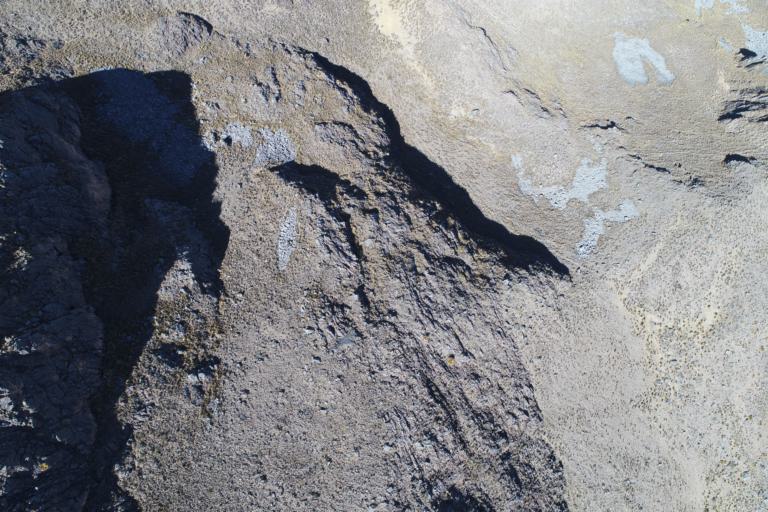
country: BO
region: La Paz
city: Viloco
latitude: -16.8065
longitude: -67.5446
